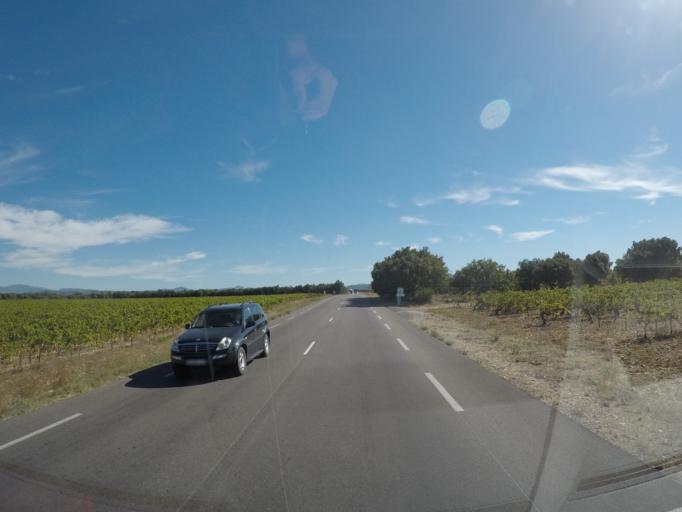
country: FR
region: Rhone-Alpes
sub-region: Departement de la Drome
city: Suze-la-Rousse
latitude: 44.2861
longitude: 4.8679
